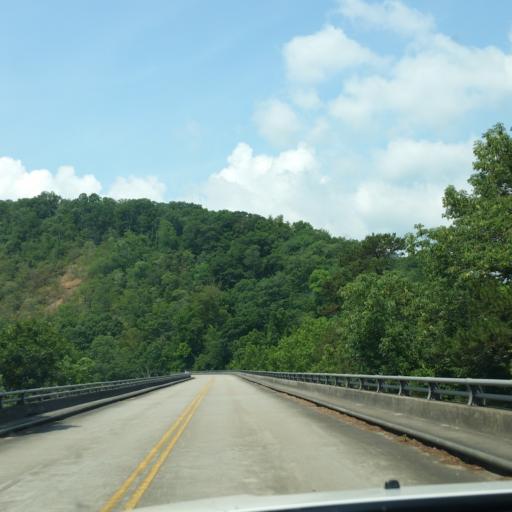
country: US
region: North Carolina
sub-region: Buncombe County
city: Bent Creek
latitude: 35.5006
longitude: -82.5904
